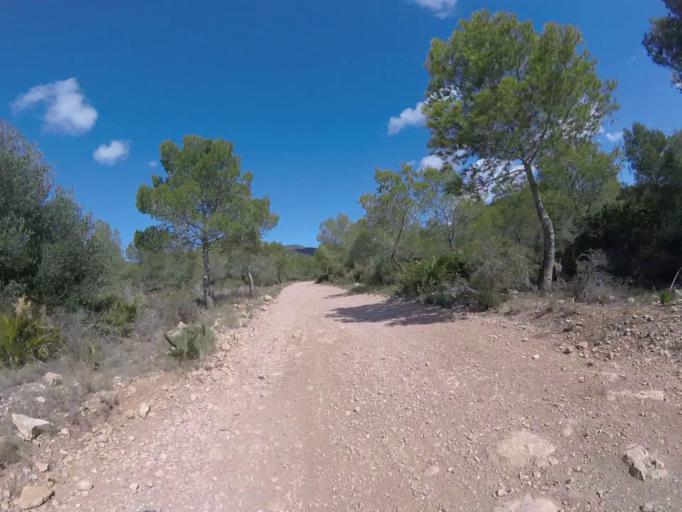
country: ES
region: Valencia
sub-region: Provincia de Castello
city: Alcoceber
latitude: 40.2903
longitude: 0.3166
